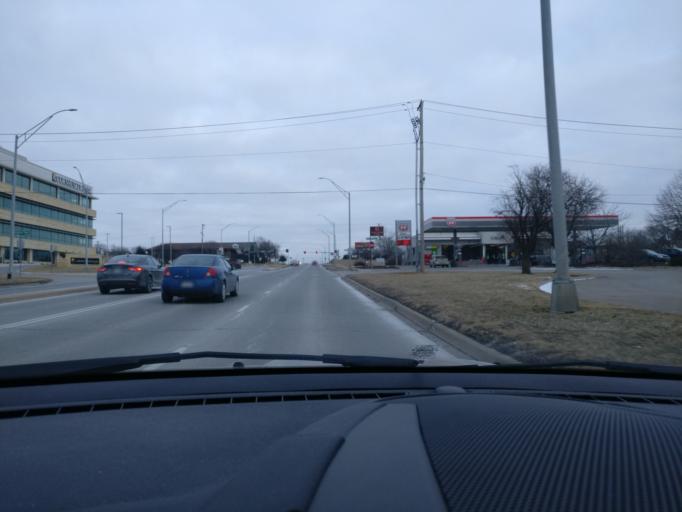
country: US
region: Nebraska
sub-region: Lancaster County
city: Lincoln
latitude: 40.8134
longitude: -96.6089
